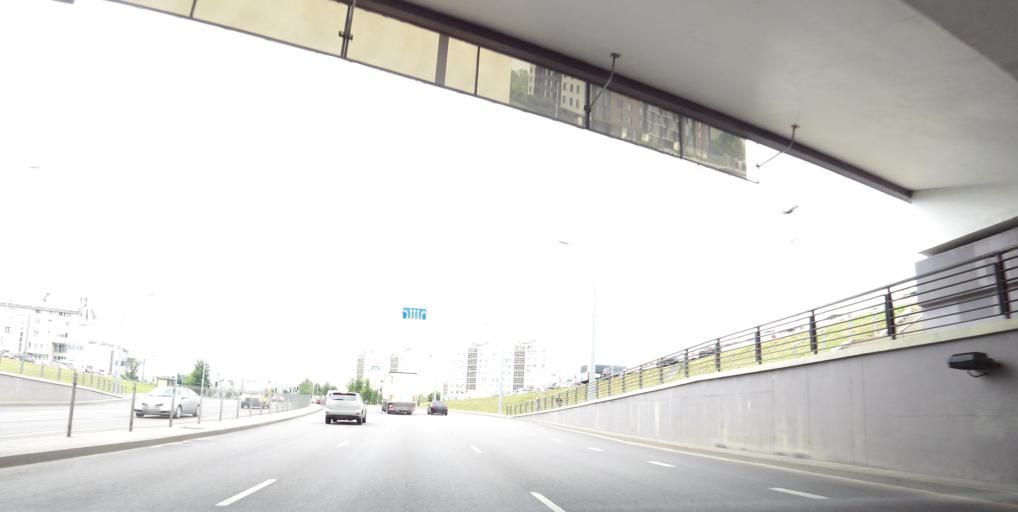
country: LT
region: Vilnius County
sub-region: Vilnius
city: Fabijoniskes
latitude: 54.7299
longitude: 25.2386
